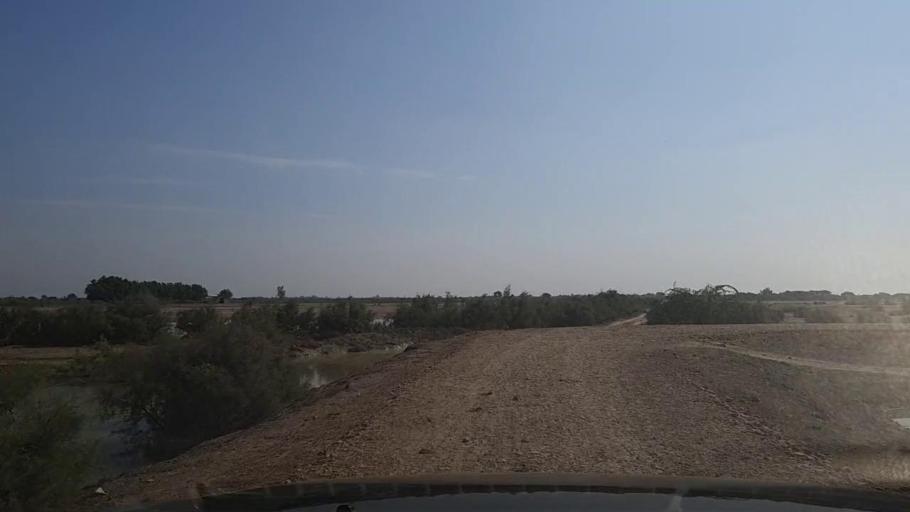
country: PK
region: Sindh
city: Gharo
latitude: 24.7083
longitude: 67.7444
